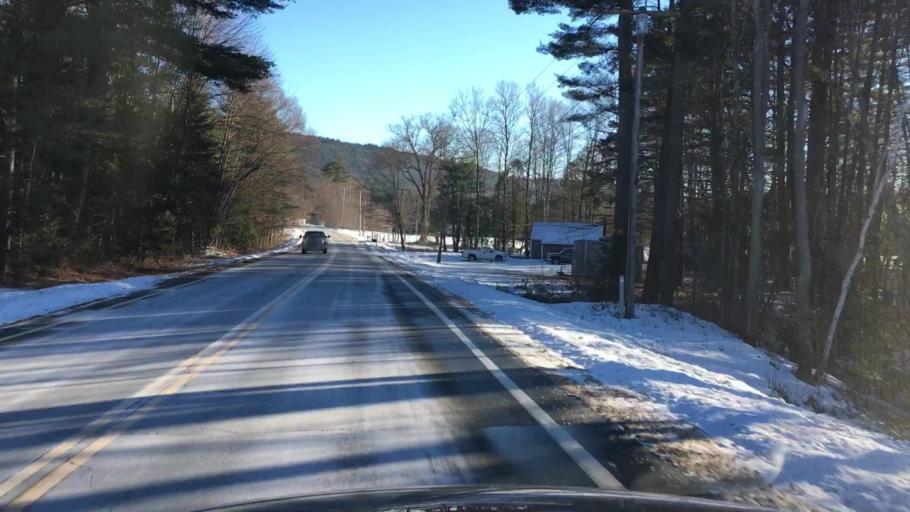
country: US
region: New Hampshire
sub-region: Grafton County
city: Woodsville
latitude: 44.2508
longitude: -72.0483
